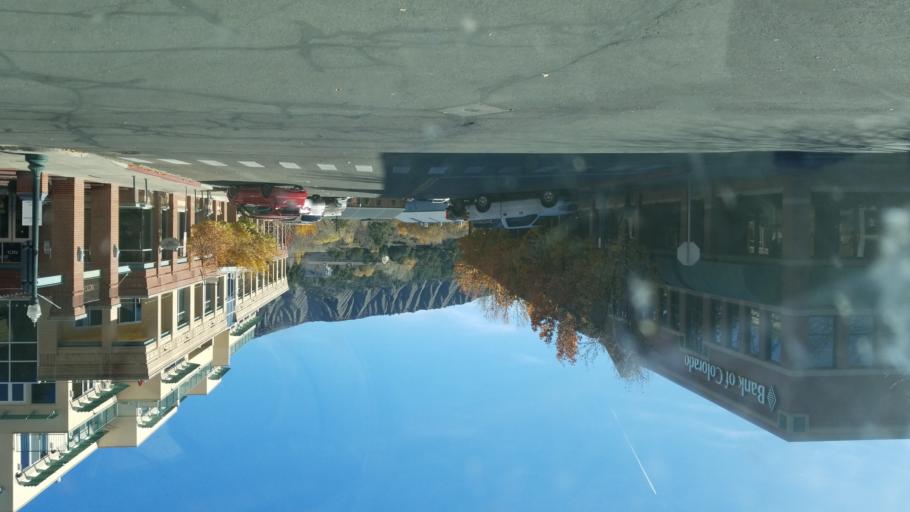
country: US
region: Colorado
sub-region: La Plata County
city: Durango
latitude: 37.2766
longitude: -107.8795
